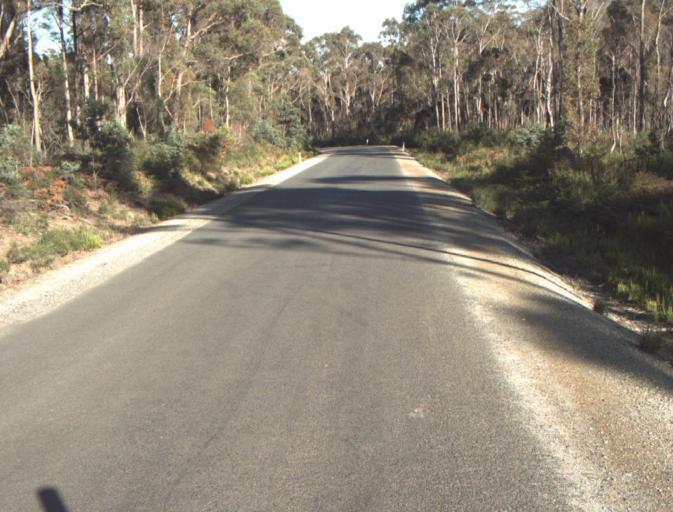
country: AU
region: Tasmania
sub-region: Launceston
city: Mayfield
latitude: -41.3362
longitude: 147.1950
